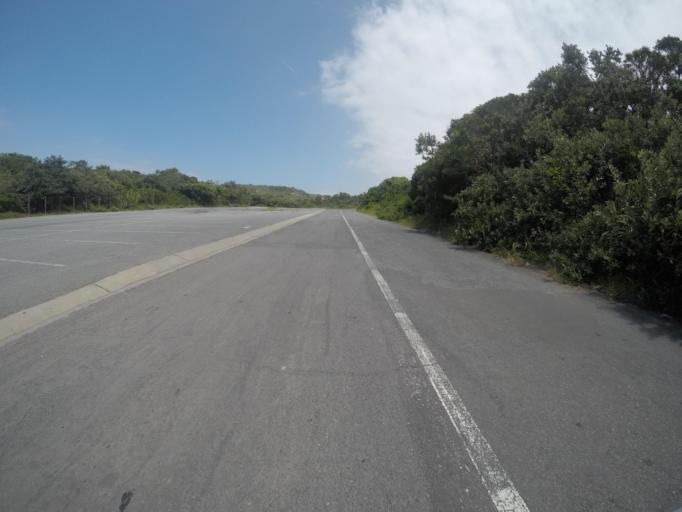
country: ZA
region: Eastern Cape
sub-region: Buffalo City Metropolitan Municipality
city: East London
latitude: -32.9950
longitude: 27.9477
